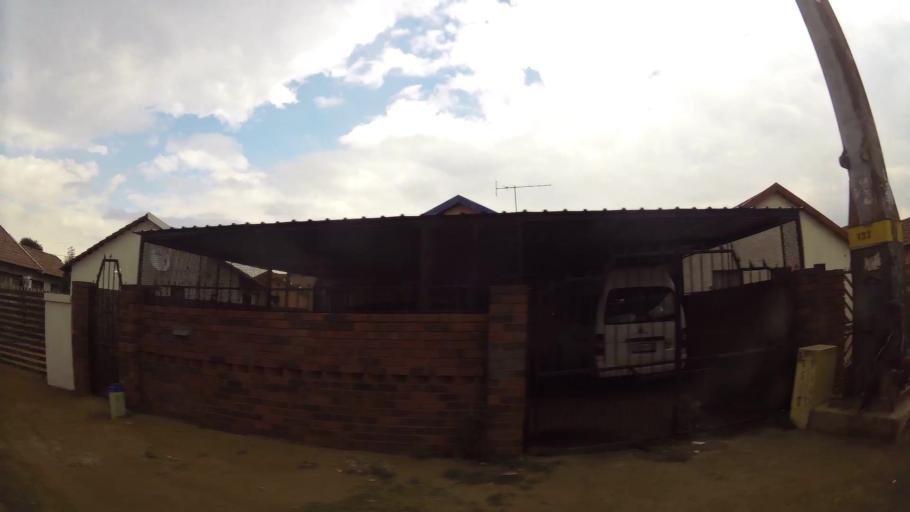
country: ZA
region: Gauteng
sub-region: Ekurhuleni Metropolitan Municipality
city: Germiston
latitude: -26.3695
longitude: 28.1601
